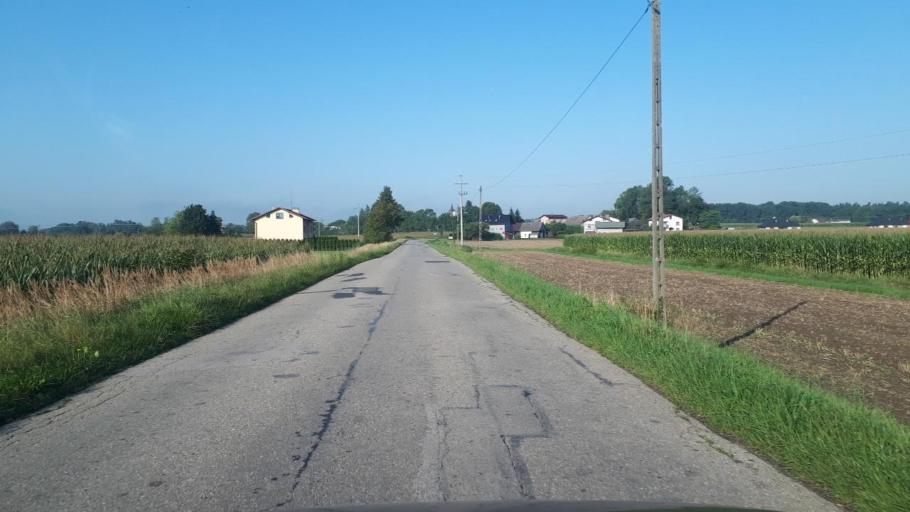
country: PL
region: Silesian Voivodeship
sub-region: Powiat cieszynski
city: Chybie
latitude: 49.8763
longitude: 18.8675
